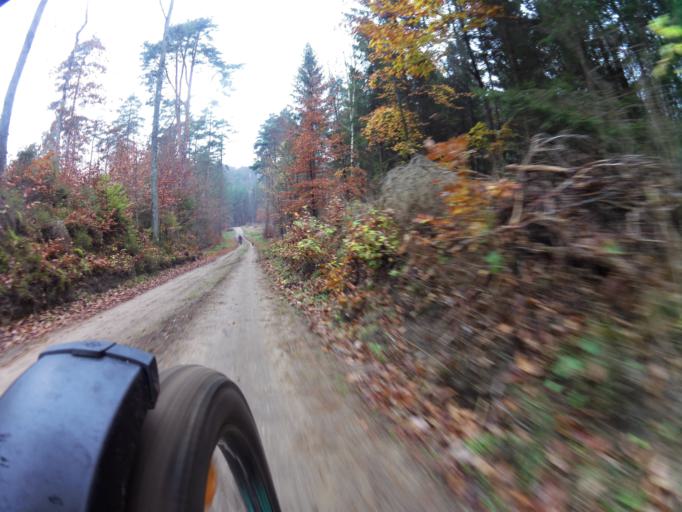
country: PL
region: Pomeranian Voivodeship
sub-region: Powiat wejherowski
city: Orle
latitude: 54.7022
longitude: 18.1550
